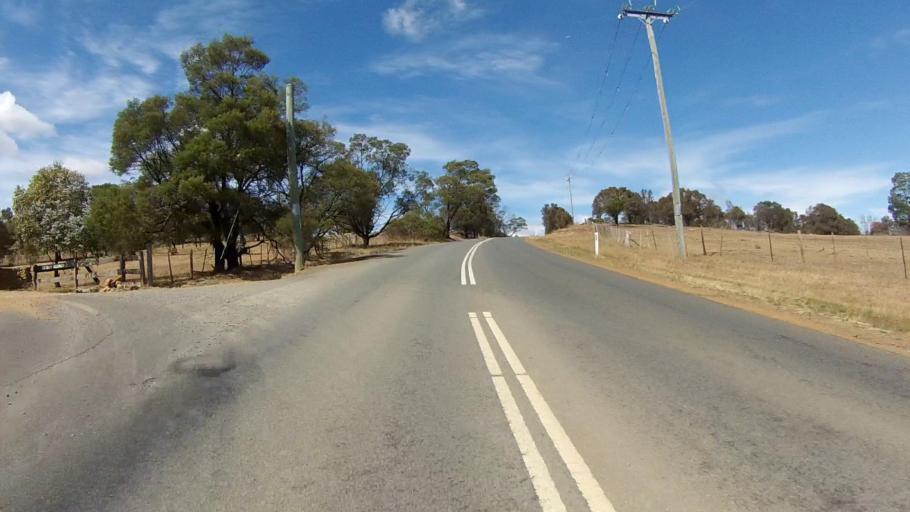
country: AU
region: Tasmania
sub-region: Brighton
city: Bridgewater
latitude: -42.7063
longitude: 147.2705
